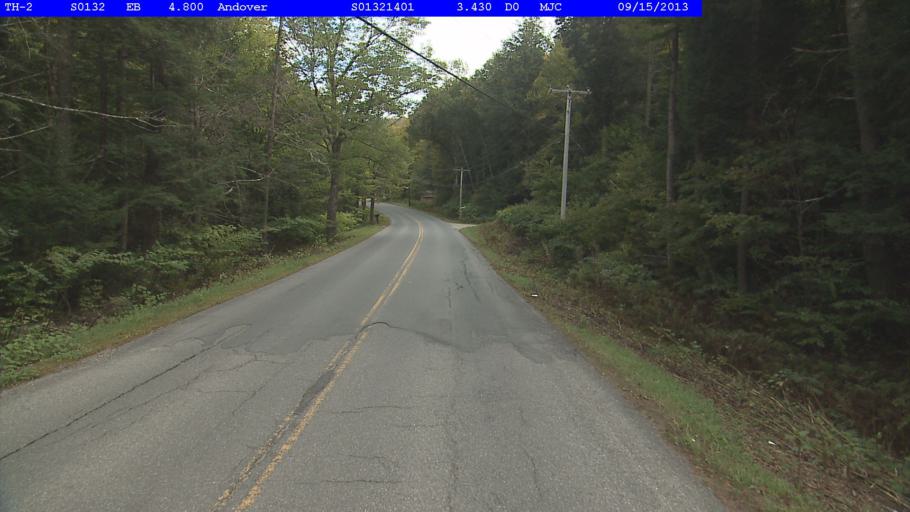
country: US
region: Vermont
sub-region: Windsor County
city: Chester
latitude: 43.2803
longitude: -72.7070
